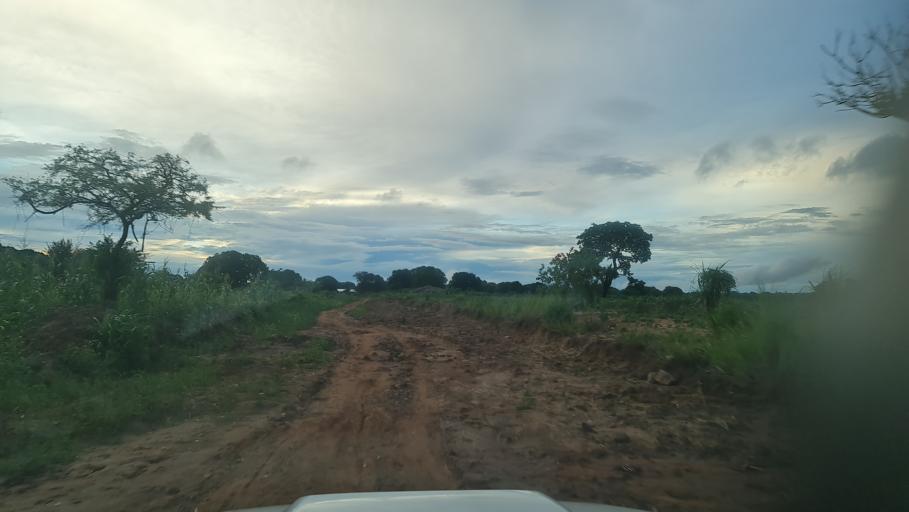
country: MZ
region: Nampula
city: Nacala
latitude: -14.7411
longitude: 39.9450
